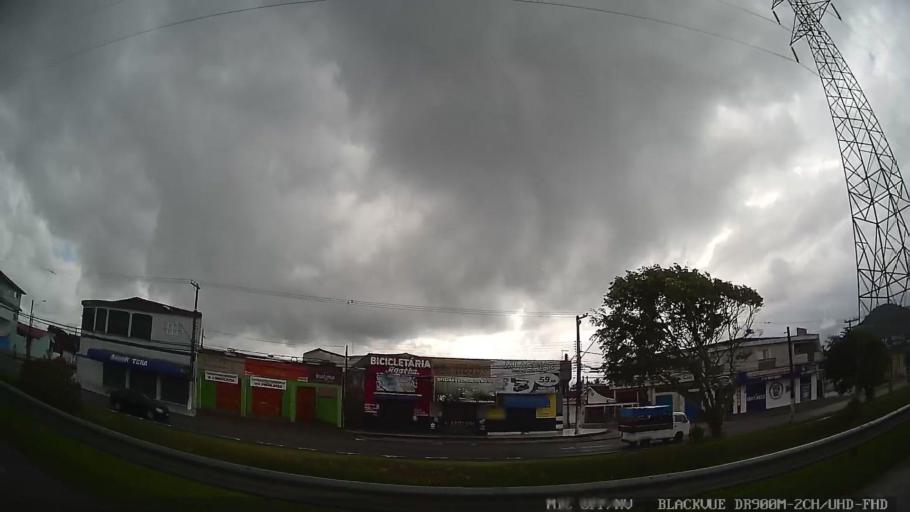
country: BR
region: Sao Paulo
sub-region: Mongagua
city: Mongagua
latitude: -24.1245
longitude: -46.6824
